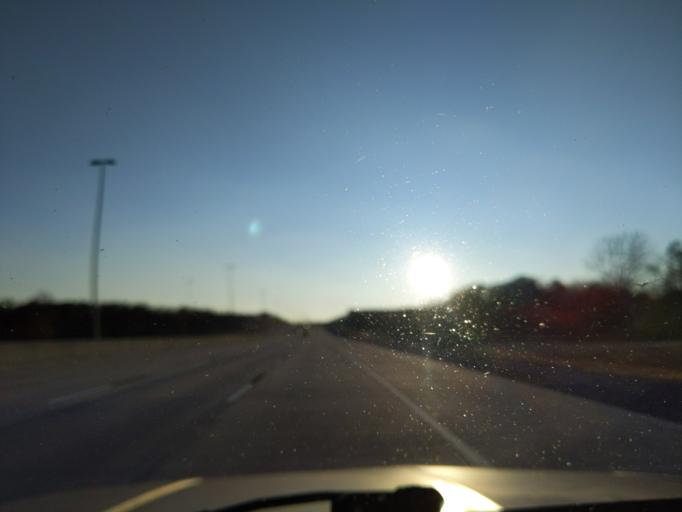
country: US
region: Oklahoma
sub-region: Creek County
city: Kellyville
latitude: 35.9625
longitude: -96.2286
